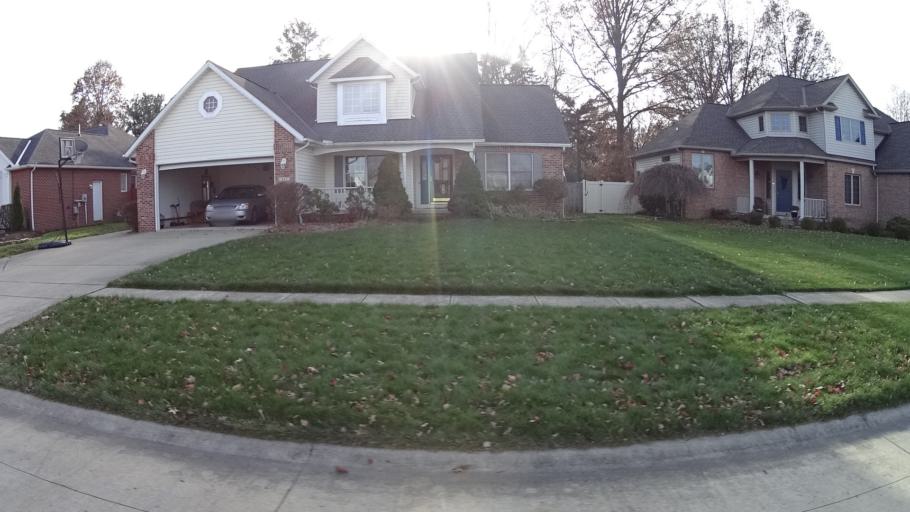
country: US
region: Ohio
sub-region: Lorain County
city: Elyria
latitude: 41.3403
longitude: -82.0853
